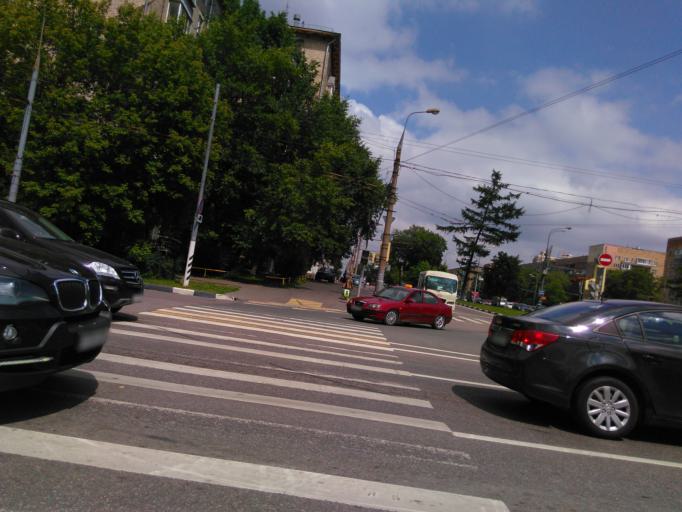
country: RU
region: Moskovskaya
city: Semenovskoye
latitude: 55.6738
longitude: 37.5236
